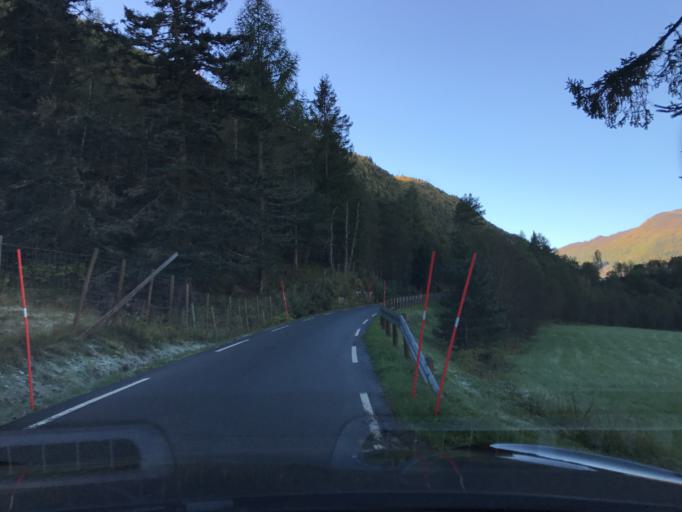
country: NO
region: More og Romsdal
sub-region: Norddal
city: Valldal
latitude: 62.3147
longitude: 7.3165
